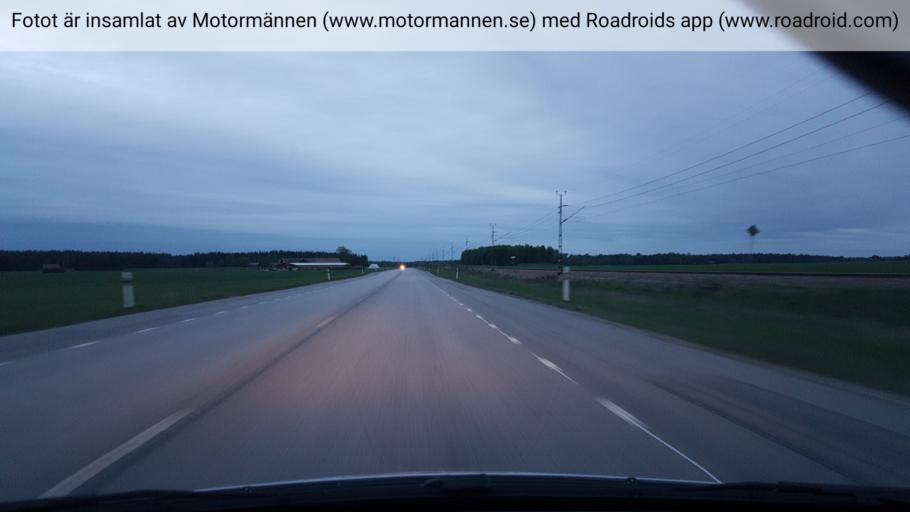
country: SE
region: Vaestmanland
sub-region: Sala Kommun
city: Sala
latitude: 59.9279
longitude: 16.6904
